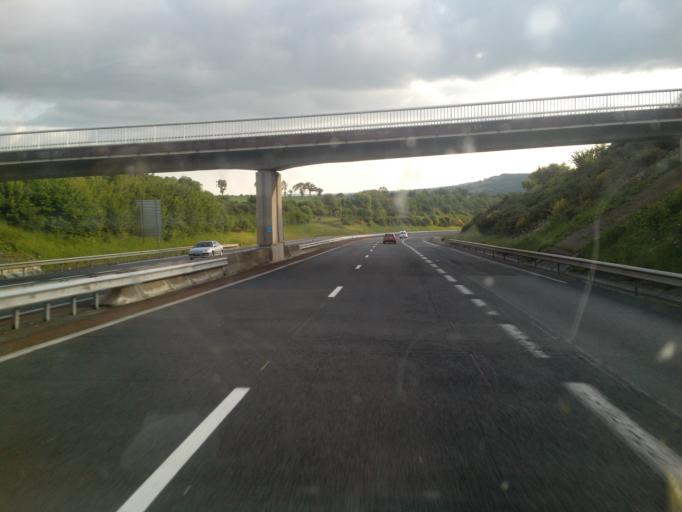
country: FR
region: Lower Normandy
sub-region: Departement de la Manche
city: Tessy-sur-Vire
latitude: 48.9501
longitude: -1.0105
